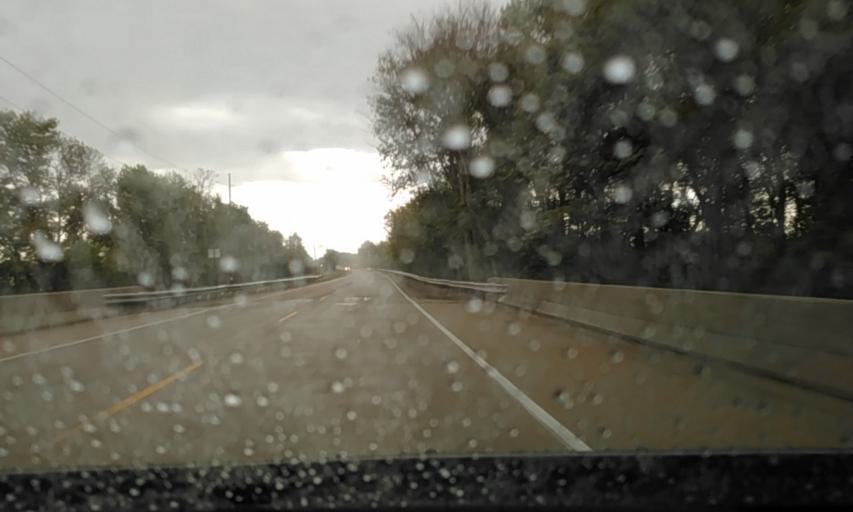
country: US
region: Illinois
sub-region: Madison County
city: Troy
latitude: 38.7164
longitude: -89.8287
